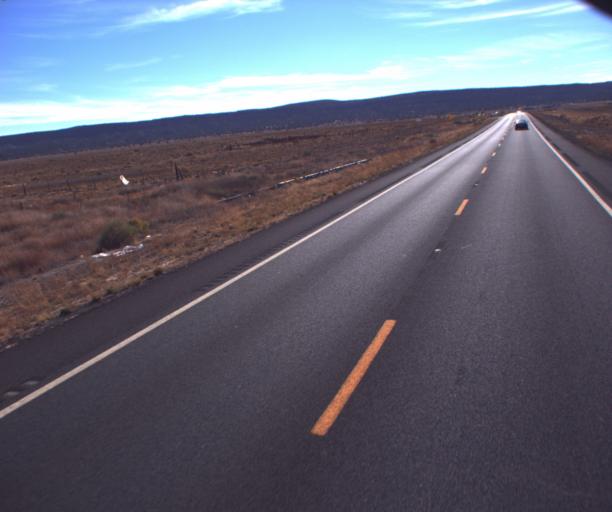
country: US
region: Arizona
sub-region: Coconino County
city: Kaibito
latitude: 36.4755
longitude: -110.7002
